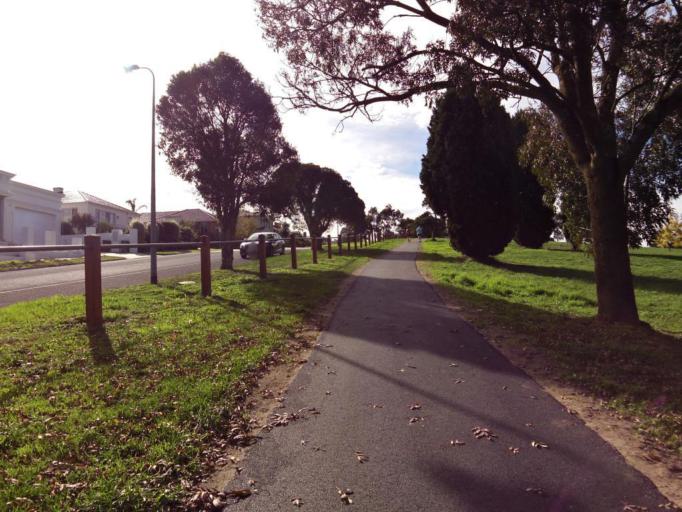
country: AU
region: Victoria
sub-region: Manningham
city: Doncaster
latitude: -37.7749
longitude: 145.1333
